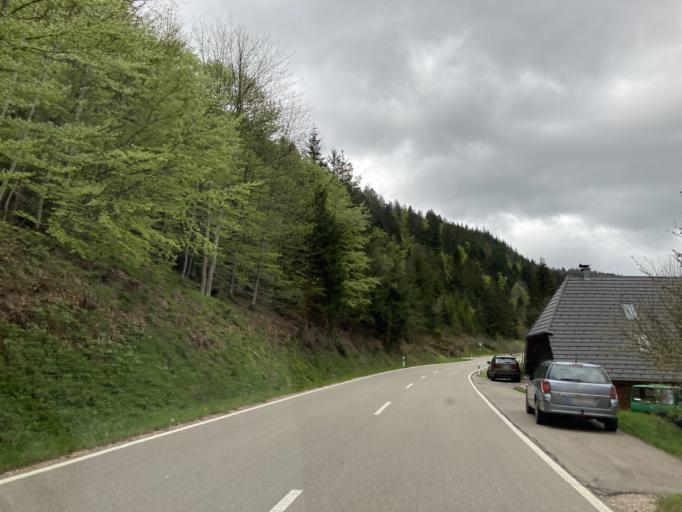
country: DE
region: Baden-Wuerttemberg
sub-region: Freiburg Region
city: Schonach im Schwarzwald
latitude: 48.1401
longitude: 8.1588
